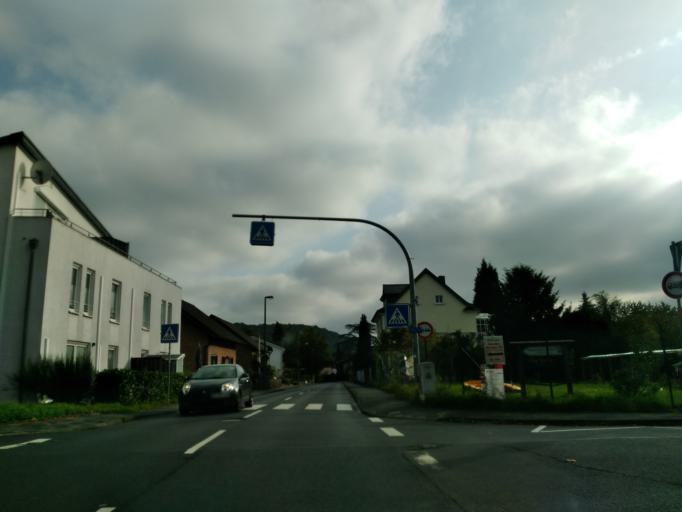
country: DE
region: North Rhine-Westphalia
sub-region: Regierungsbezirk Koln
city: Konigswinter
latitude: 50.6989
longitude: 7.1855
